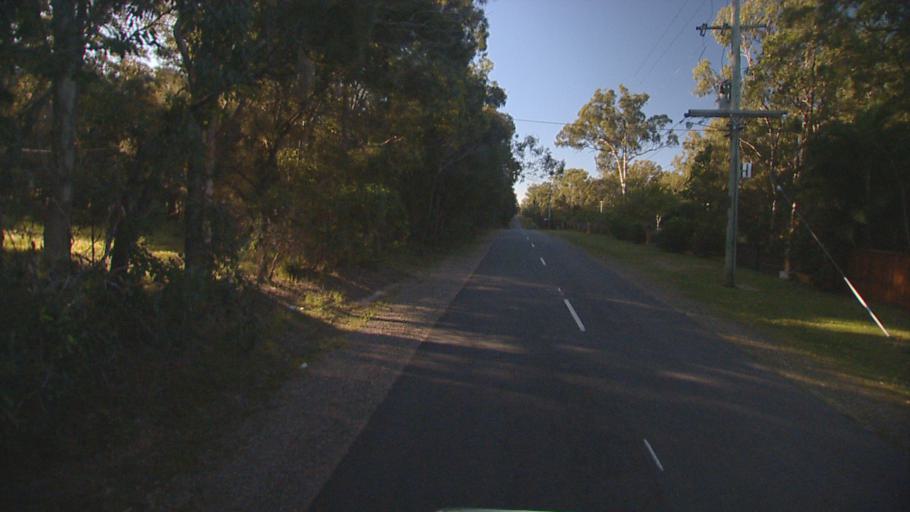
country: AU
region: Queensland
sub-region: Gold Coast
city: Yatala
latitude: -27.6840
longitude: 153.2745
